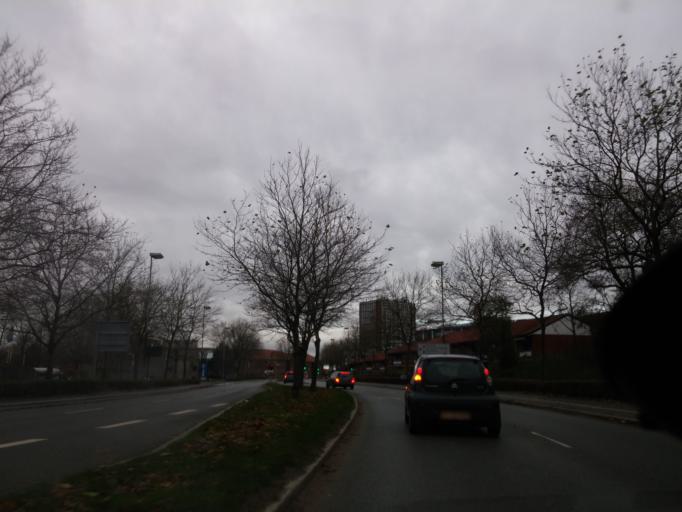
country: DK
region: South Denmark
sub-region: Odense Kommune
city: Odense
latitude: 55.4032
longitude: 10.3900
